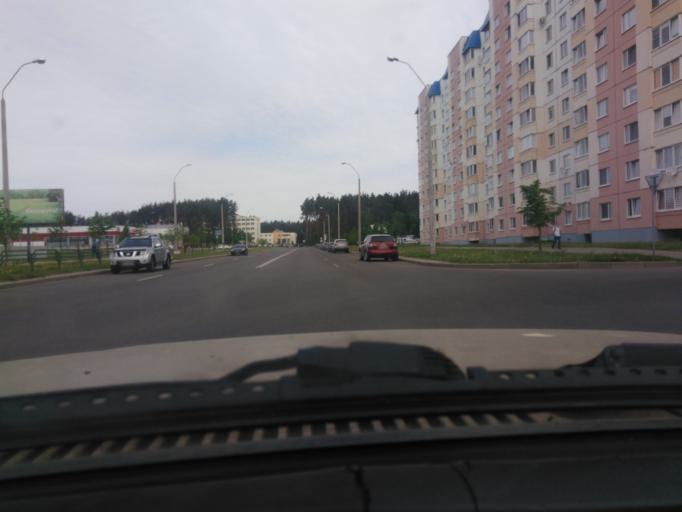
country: BY
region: Mogilev
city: Mahilyow
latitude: 53.9156
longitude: 30.2837
